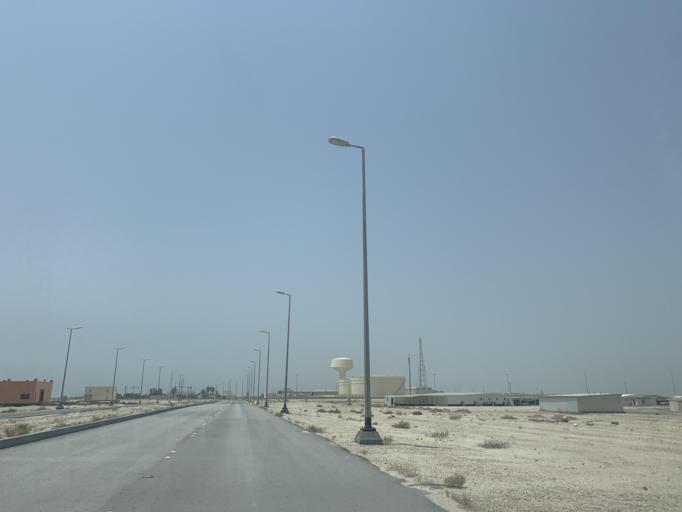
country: BH
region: Central Governorate
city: Dar Kulayb
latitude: 25.8426
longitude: 50.5887
